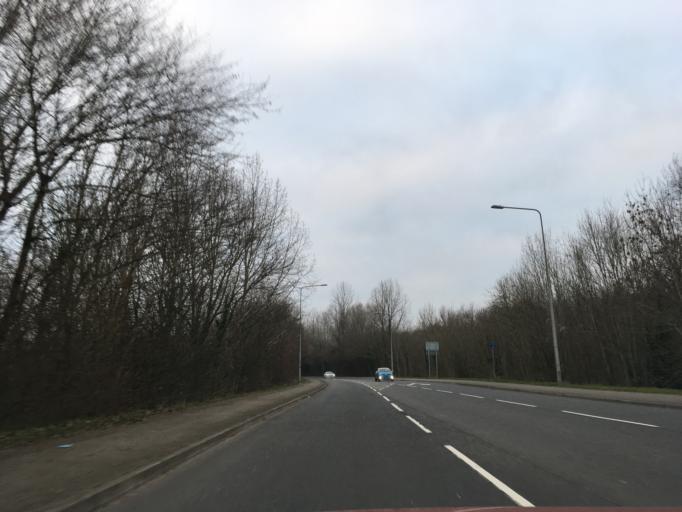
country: GB
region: Wales
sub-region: Newport
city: Newport
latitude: 51.5886
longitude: -3.0511
